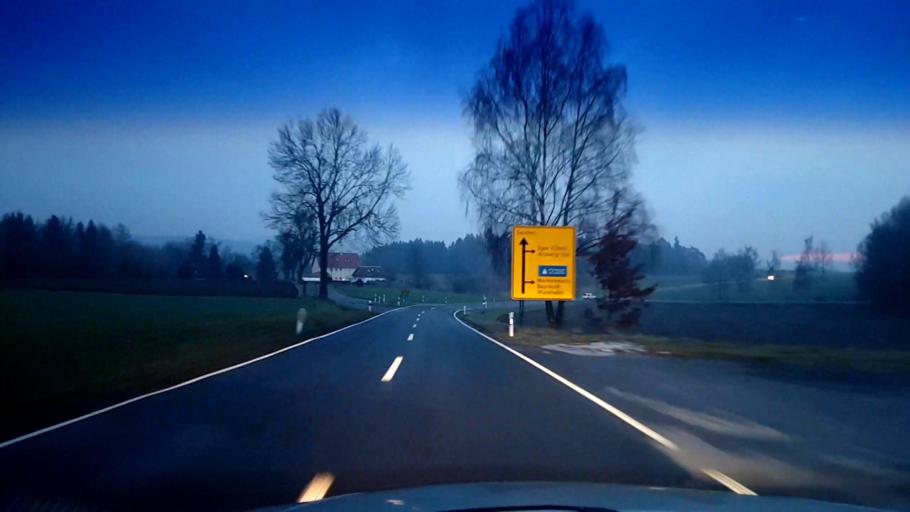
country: DE
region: Bavaria
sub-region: Upper Franconia
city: Arzberg
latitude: 50.0481
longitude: 12.1687
